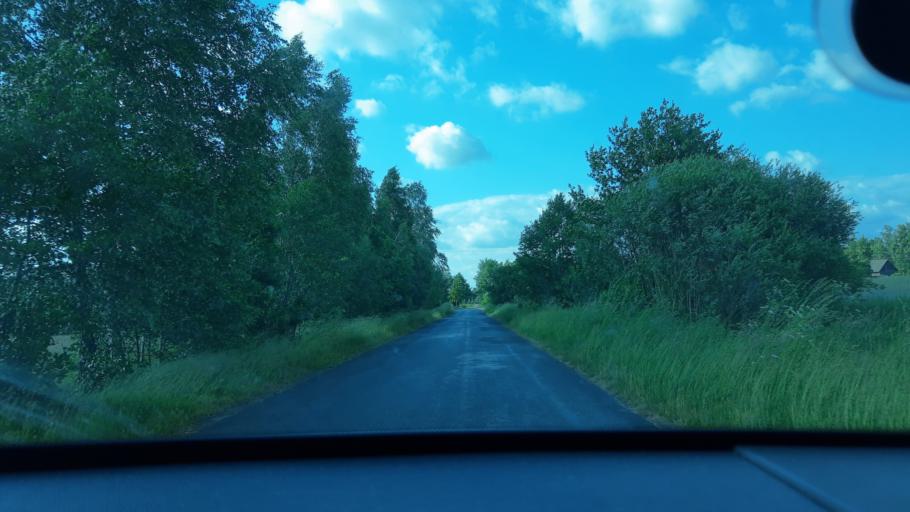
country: PL
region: Lodz Voivodeship
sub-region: Powiat zdunskowolski
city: Zapolice
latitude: 51.5319
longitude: 18.8371
